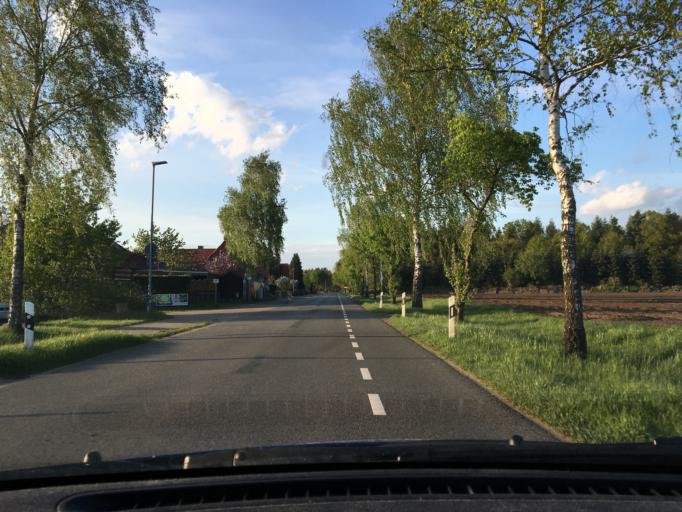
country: DE
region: Lower Saxony
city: Wietzendorf
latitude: 52.9287
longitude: 9.9801
